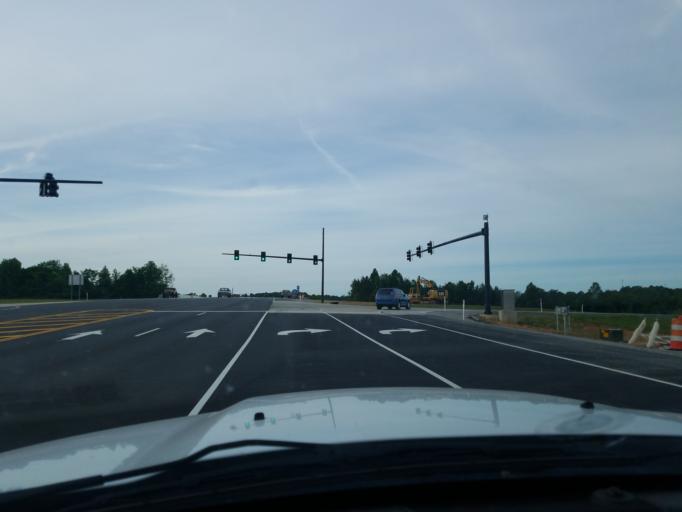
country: US
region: Tennessee
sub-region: Putnam County
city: Baxter
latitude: 36.1377
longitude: -85.5790
